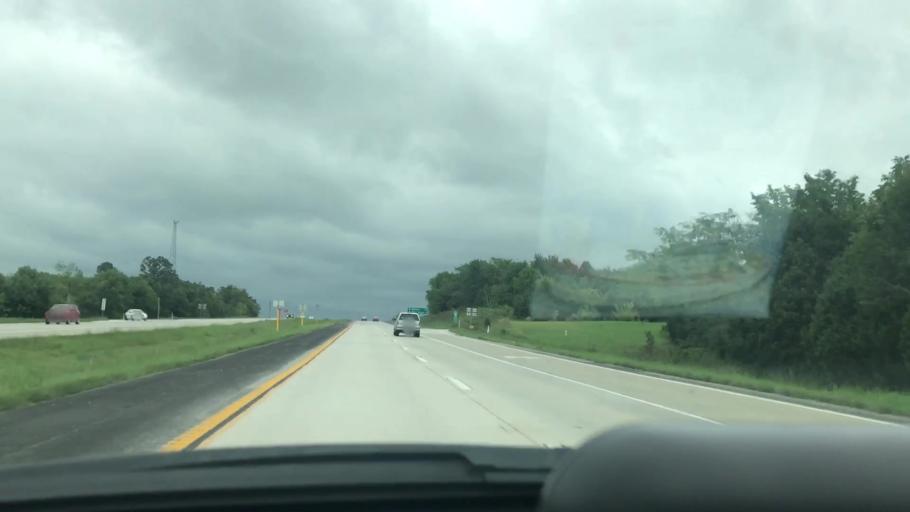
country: US
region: Missouri
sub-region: Greene County
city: Fair Grove
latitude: 37.4215
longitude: -93.1450
